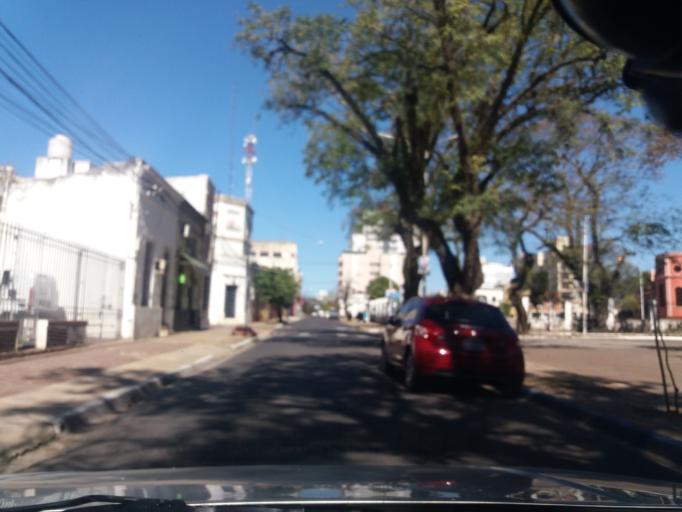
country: AR
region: Corrientes
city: Corrientes
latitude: -27.4715
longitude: -58.8394
